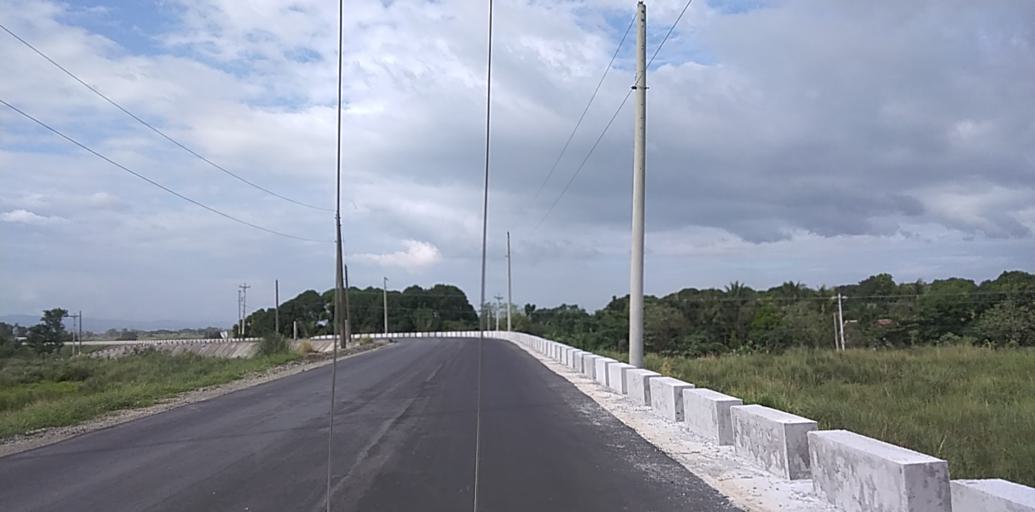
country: PH
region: Central Luzon
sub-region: Province of Pampanga
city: Porac
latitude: 15.0670
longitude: 120.5598
